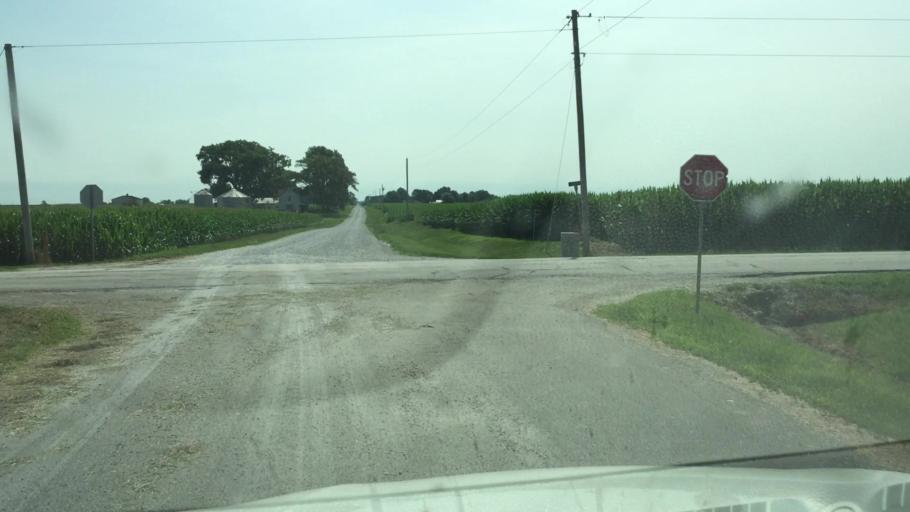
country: US
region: Illinois
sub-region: Hancock County
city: Nauvoo
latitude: 40.5072
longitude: -91.3088
